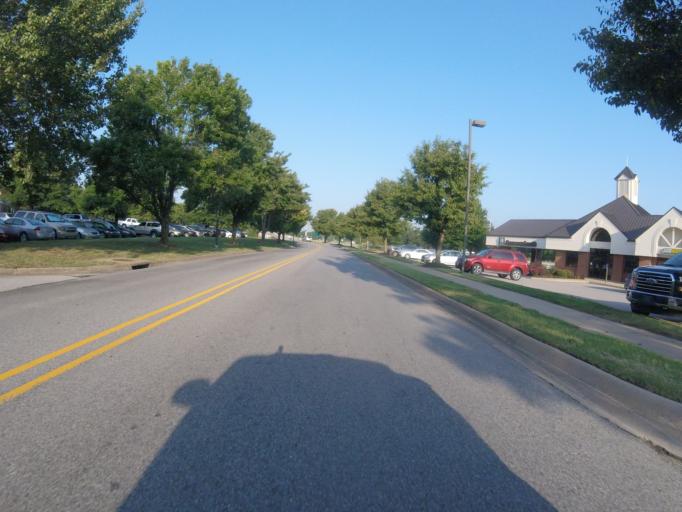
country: US
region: Arkansas
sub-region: Washington County
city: Johnson
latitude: 36.1128
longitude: -94.1559
